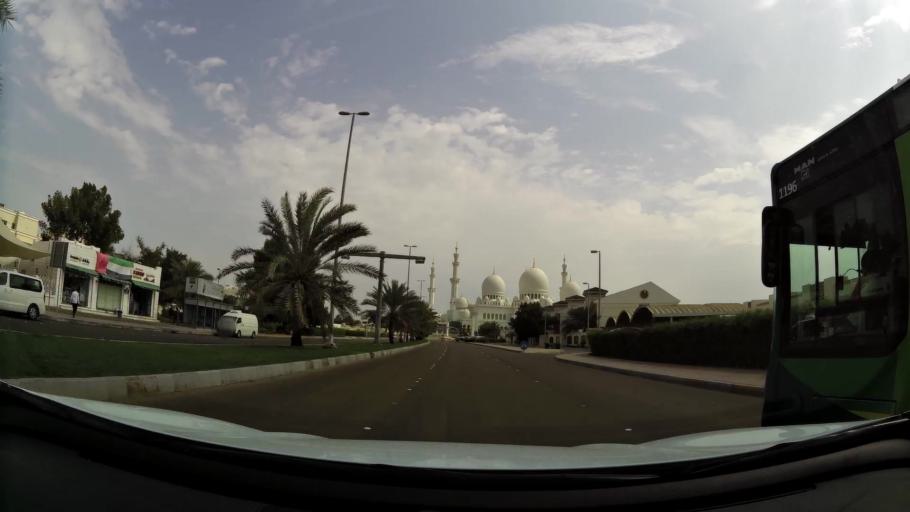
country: AE
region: Abu Dhabi
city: Abu Dhabi
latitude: 24.4133
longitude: 54.4695
